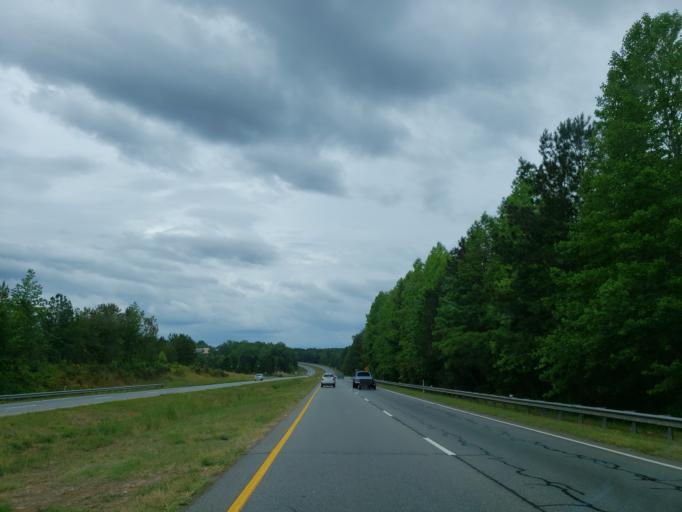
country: US
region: Georgia
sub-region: Haralson County
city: Bremen
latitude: 33.7038
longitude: -85.1591
